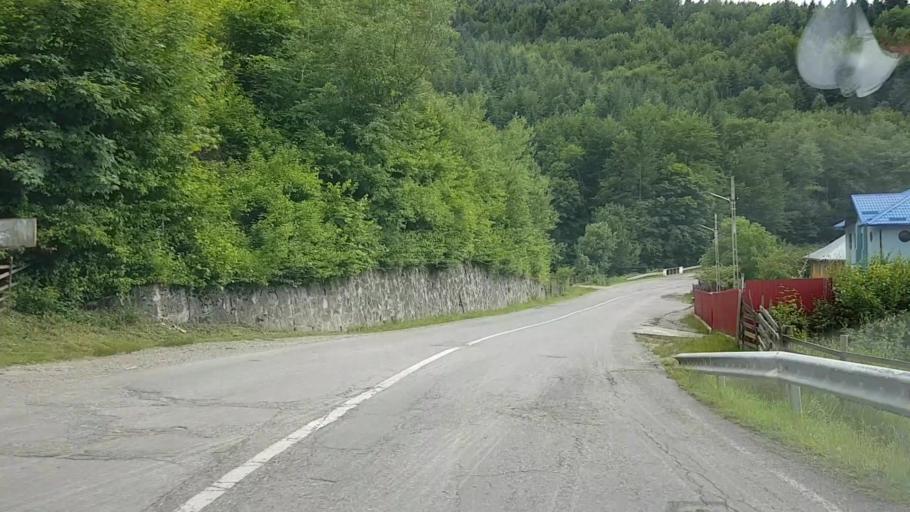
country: RO
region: Neamt
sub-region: Comuna Pangarati
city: Pangarati
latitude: 46.9904
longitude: 26.1209
